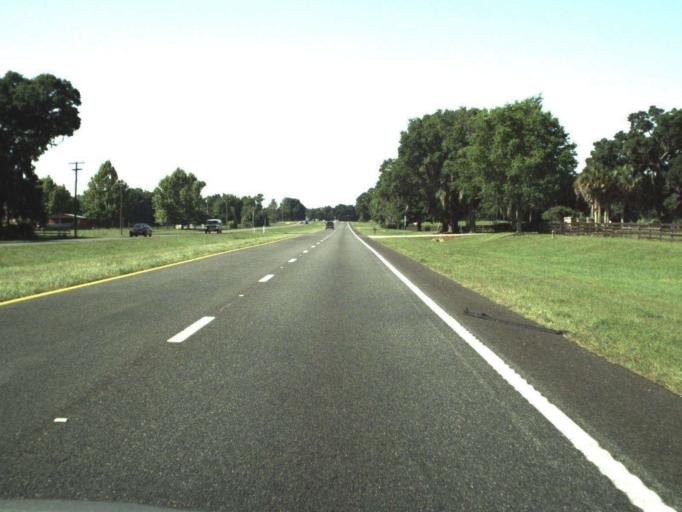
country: US
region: Florida
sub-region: Marion County
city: Citra
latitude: 29.3540
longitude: -82.1433
